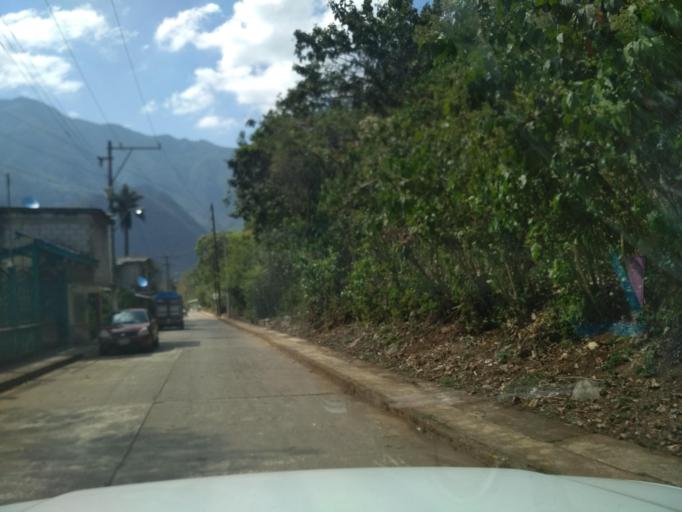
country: MX
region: Veracruz
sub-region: Tlilapan
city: Tonalixco
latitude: 18.7890
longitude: -97.0914
